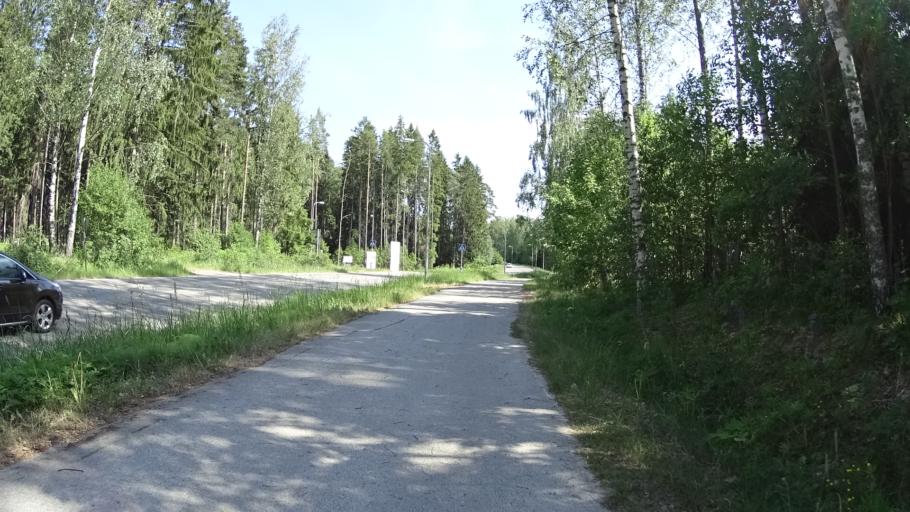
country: FI
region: Uusimaa
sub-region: Raaseporin
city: Karis
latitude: 60.0814
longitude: 23.6636
